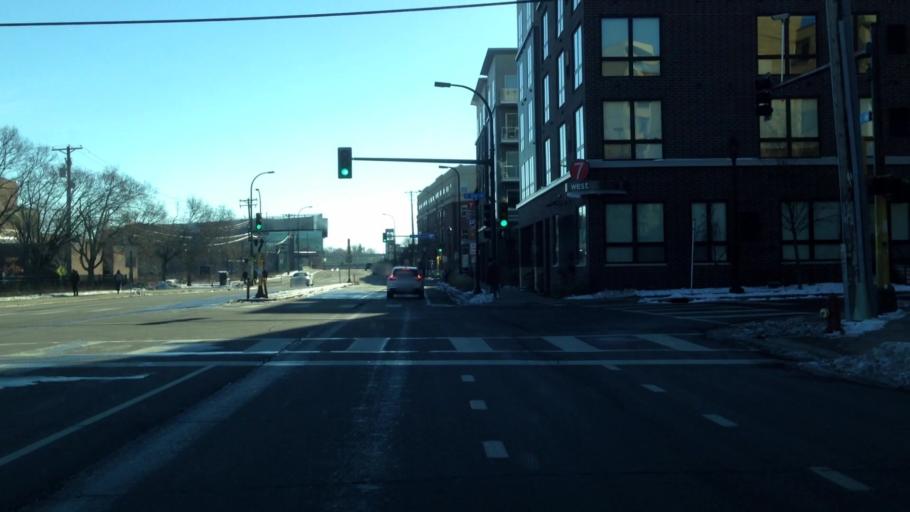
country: US
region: Minnesota
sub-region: Hennepin County
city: Minneapolis
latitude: 44.9745
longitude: -93.2460
